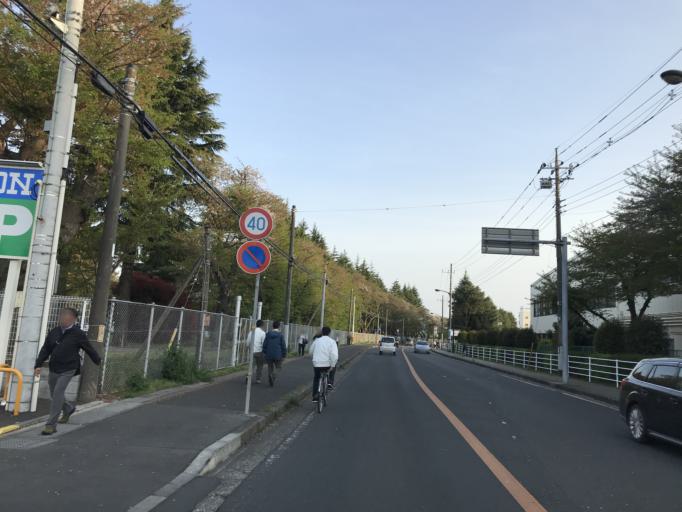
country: JP
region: Ibaraki
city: Katsuta
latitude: 36.3856
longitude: 140.5275
